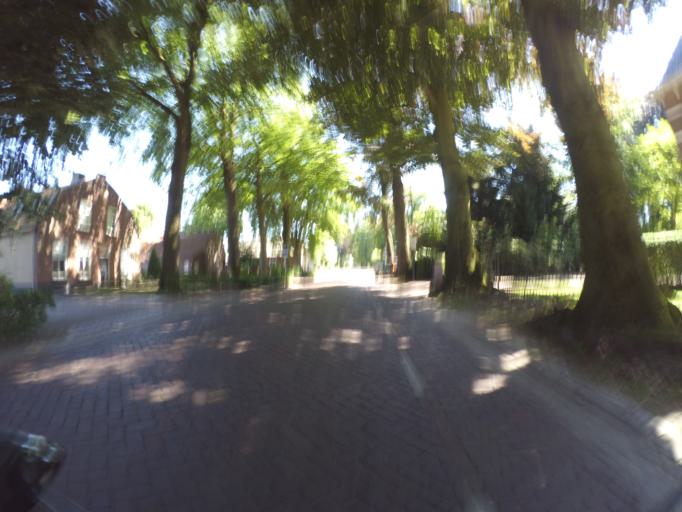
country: NL
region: North Brabant
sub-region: Gemeente Dongen
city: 's Gravenmoer
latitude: 51.6522
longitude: 4.9416
